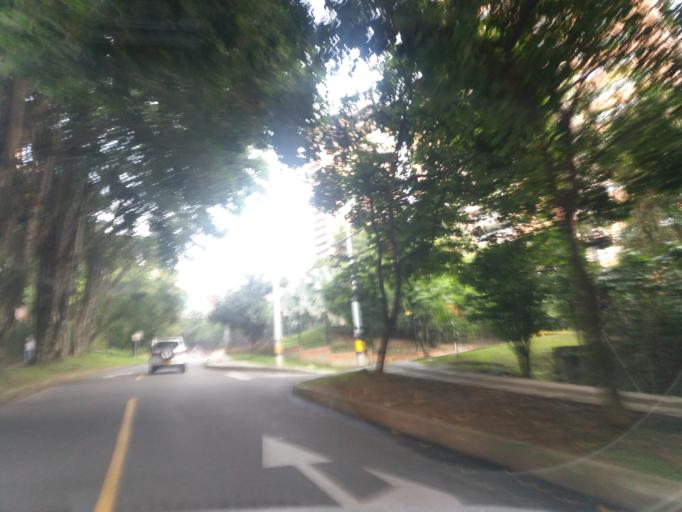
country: CO
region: Antioquia
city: Itagui
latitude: 6.2046
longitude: -75.5689
